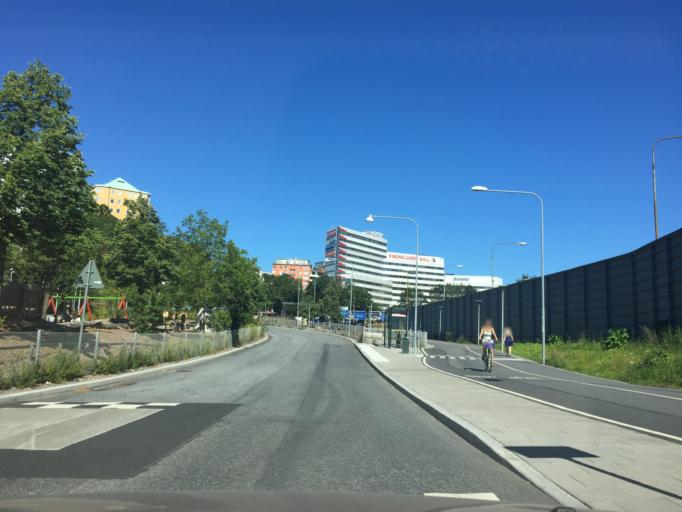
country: SE
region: Stockholm
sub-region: Stockholms Kommun
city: OEstermalm
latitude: 59.3106
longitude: 18.1059
